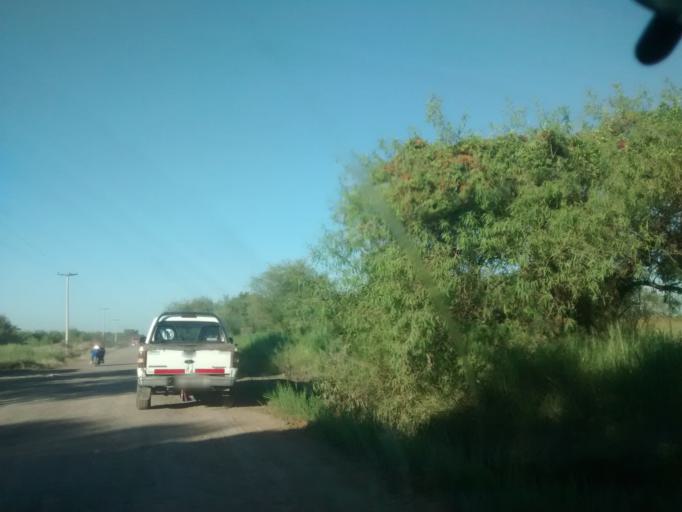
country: AR
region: Chaco
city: Resistencia
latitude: -27.4606
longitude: -59.0256
